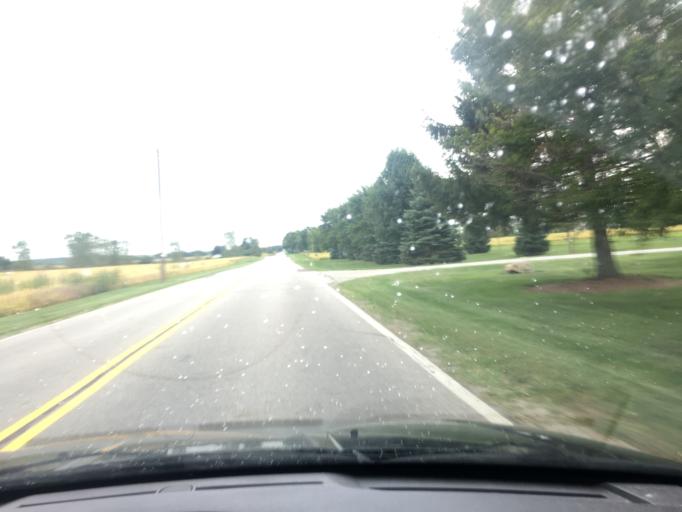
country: US
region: Ohio
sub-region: Logan County
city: West Liberty
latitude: 40.1833
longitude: -83.6925
